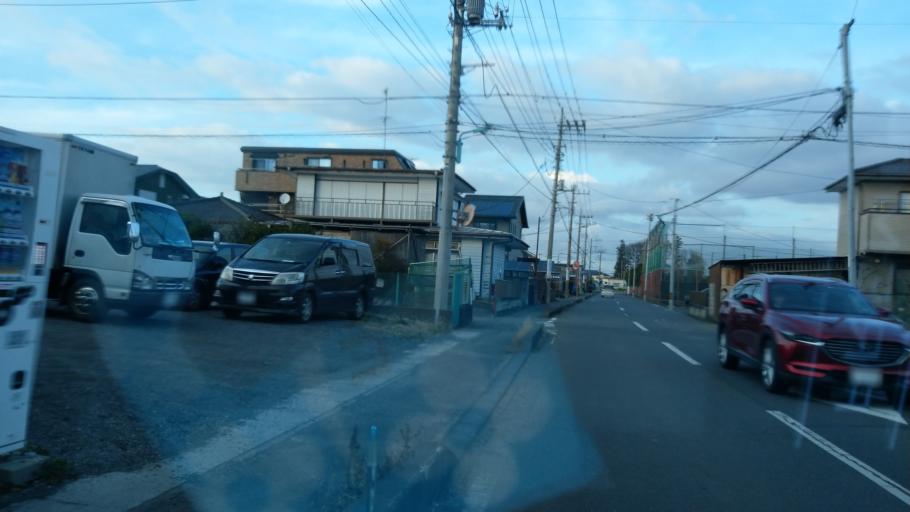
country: JP
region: Saitama
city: Yono
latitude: 35.8947
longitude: 139.5874
